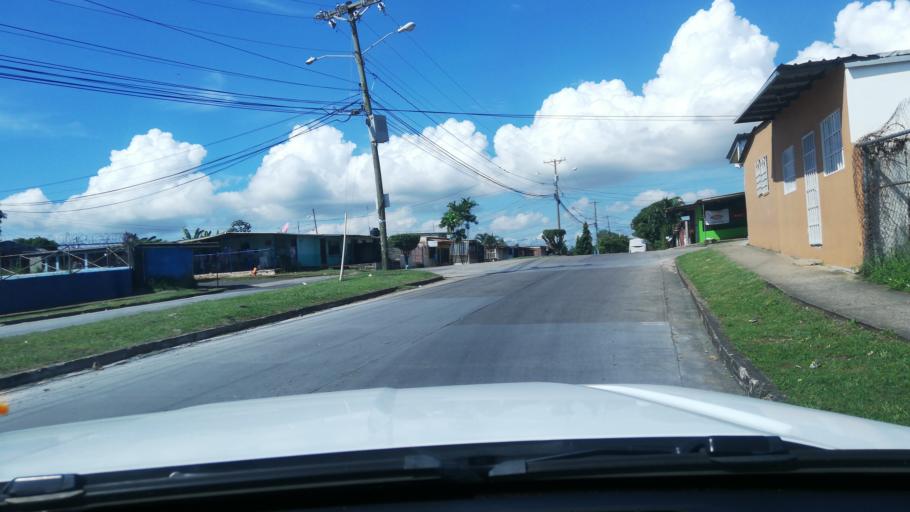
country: PA
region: Panama
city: Tocumen
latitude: 9.0796
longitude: -79.3577
